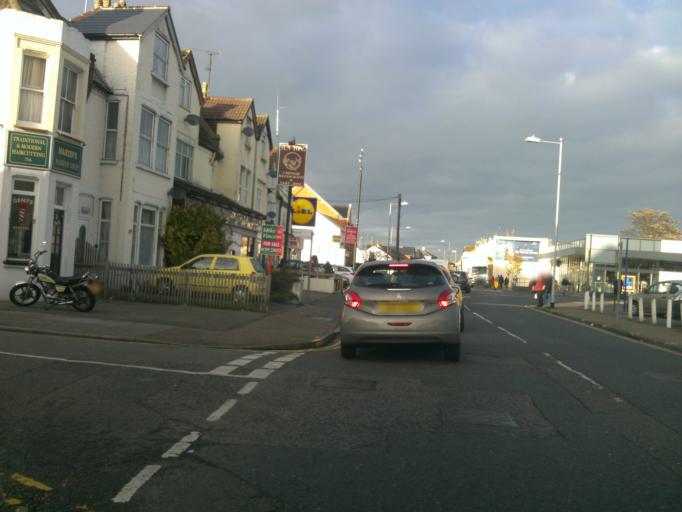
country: GB
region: England
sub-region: Essex
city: Clacton-on-Sea
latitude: 51.7922
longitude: 1.1482
